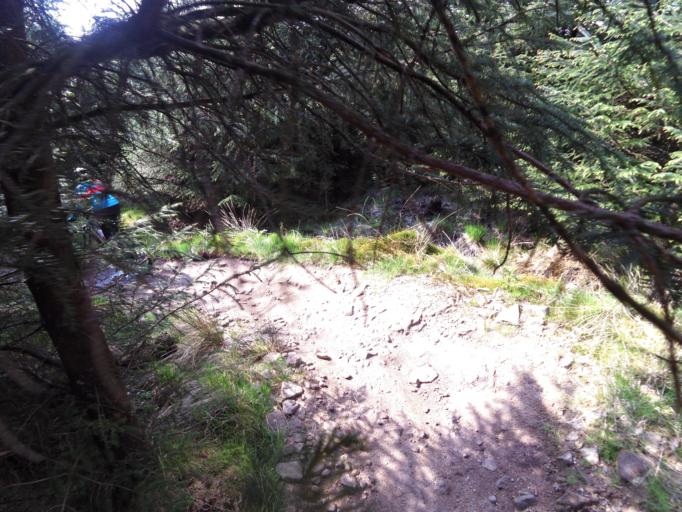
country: GB
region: England
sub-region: North Yorkshire
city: Settle
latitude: 54.0235
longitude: -2.3745
